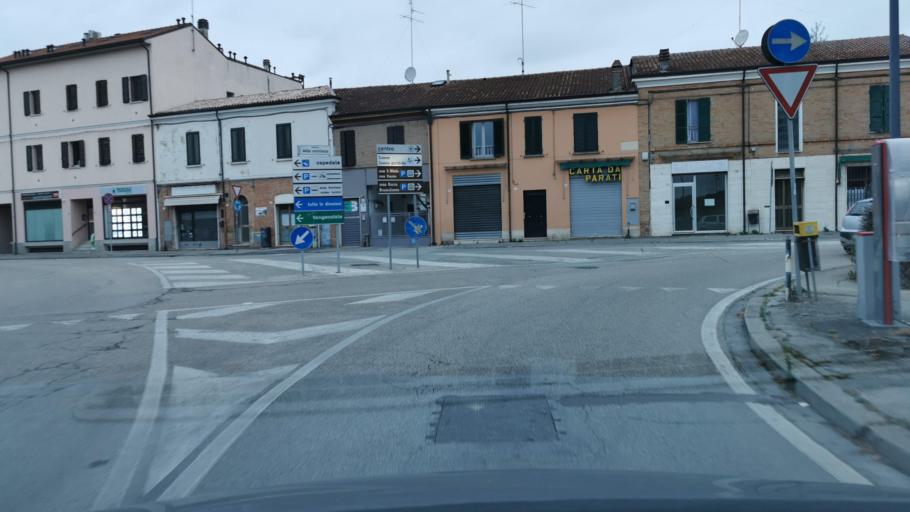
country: IT
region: Emilia-Romagna
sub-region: Provincia di Ravenna
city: Ravenna
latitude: 44.4151
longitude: 12.1888
